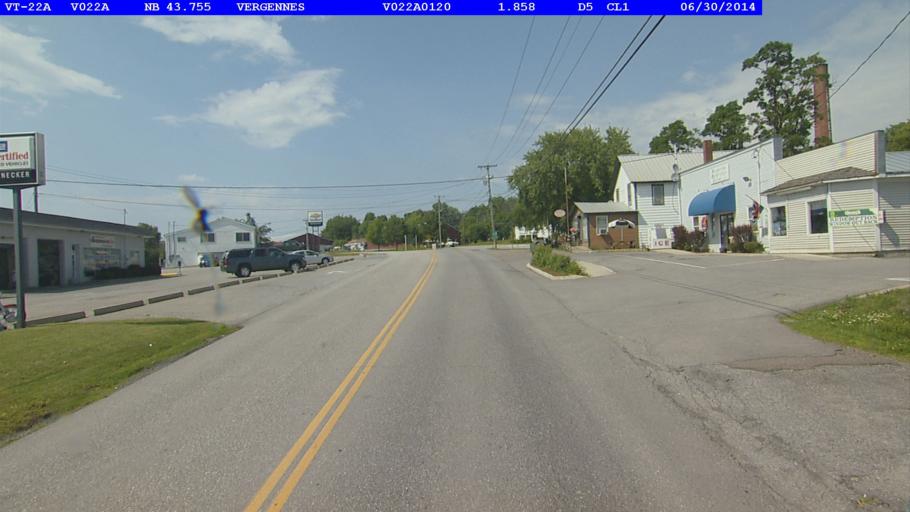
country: US
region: Vermont
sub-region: Addison County
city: Vergennes
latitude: 44.1756
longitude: -73.2458
